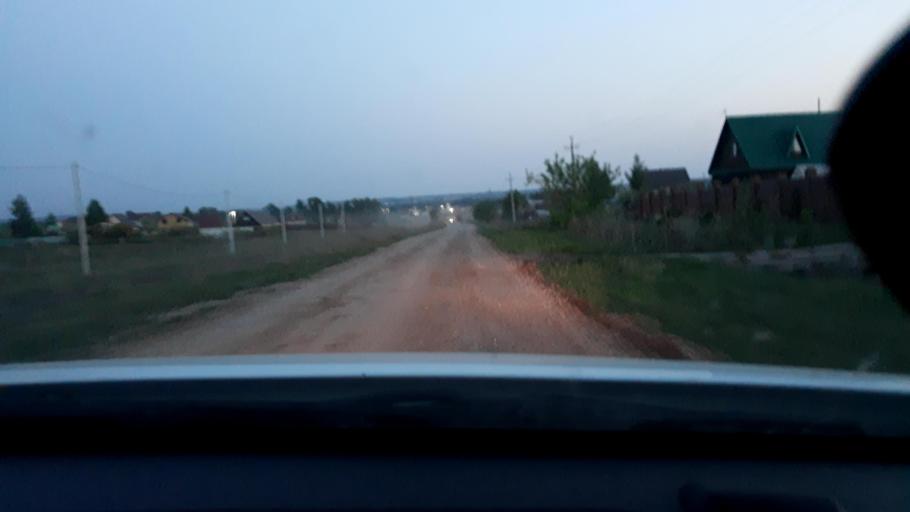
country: RU
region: Bashkortostan
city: Avdon
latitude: 54.5184
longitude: 55.8250
